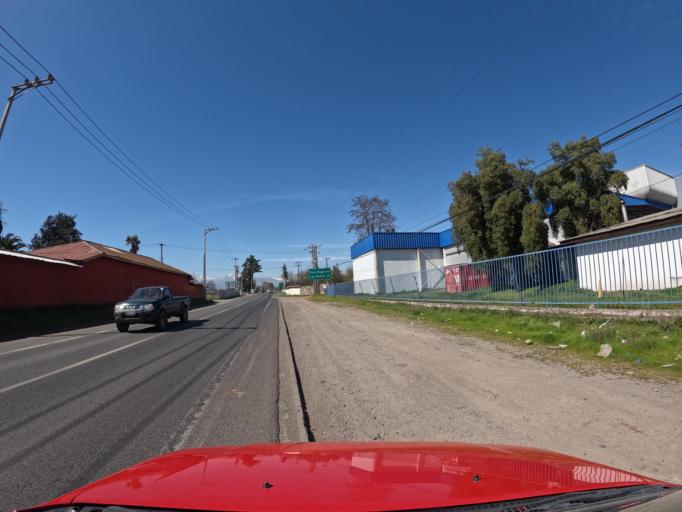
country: CL
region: Maule
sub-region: Provincia de Curico
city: Teno
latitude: -34.9614
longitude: -71.0950
